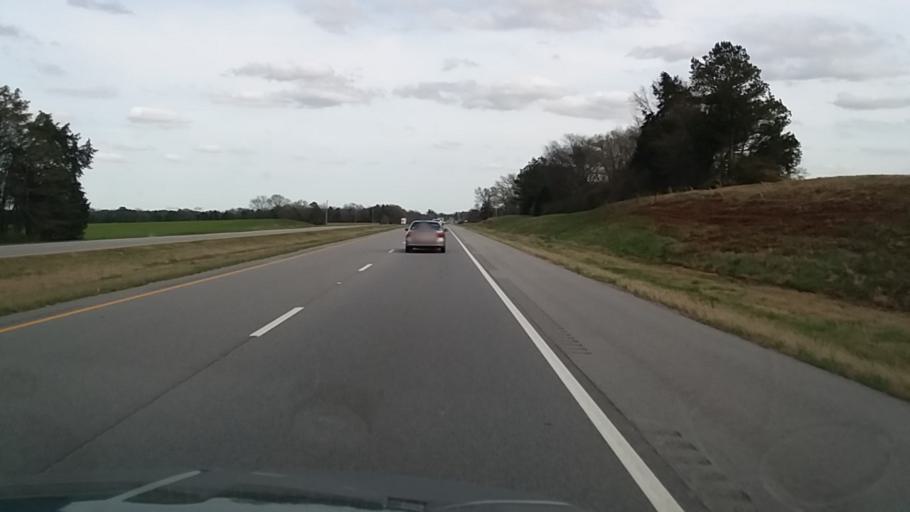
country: US
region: Alabama
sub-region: Lawrence County
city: Town Creek
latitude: 34.6824
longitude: -87.4646
